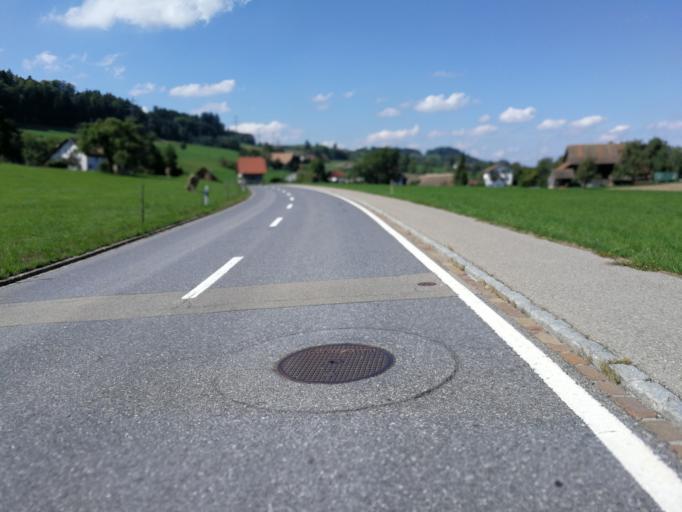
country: CH
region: Zurich
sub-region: Bezirk Horgen
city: Au
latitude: 47.2236
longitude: 8.6284
